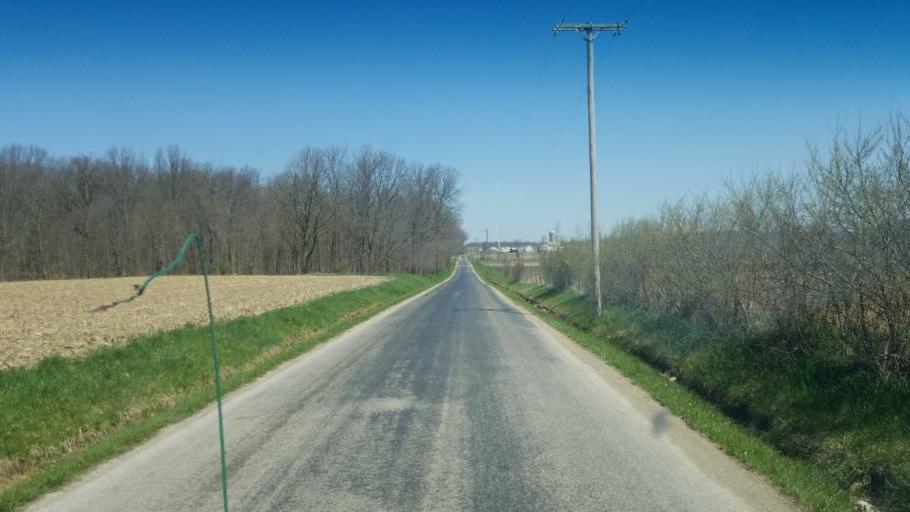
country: US
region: Ohio
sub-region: Richland County
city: Lincoln Heights
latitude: 40.8962
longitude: -82.4554
